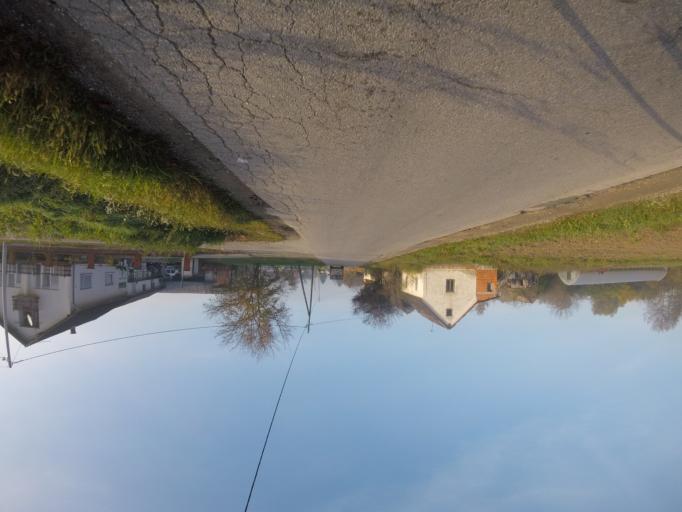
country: HR
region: Zagrebacka
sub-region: Grad Velika Gorica
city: Velika Gorica
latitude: 45.7146
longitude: 16.1199
